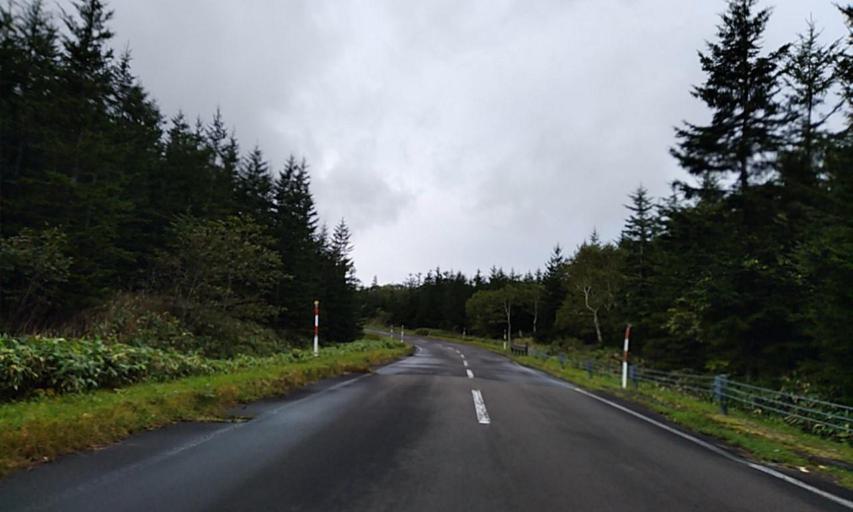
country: JP
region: Hokkaido
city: Abashiri
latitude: 43.6071
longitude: 144.5888
